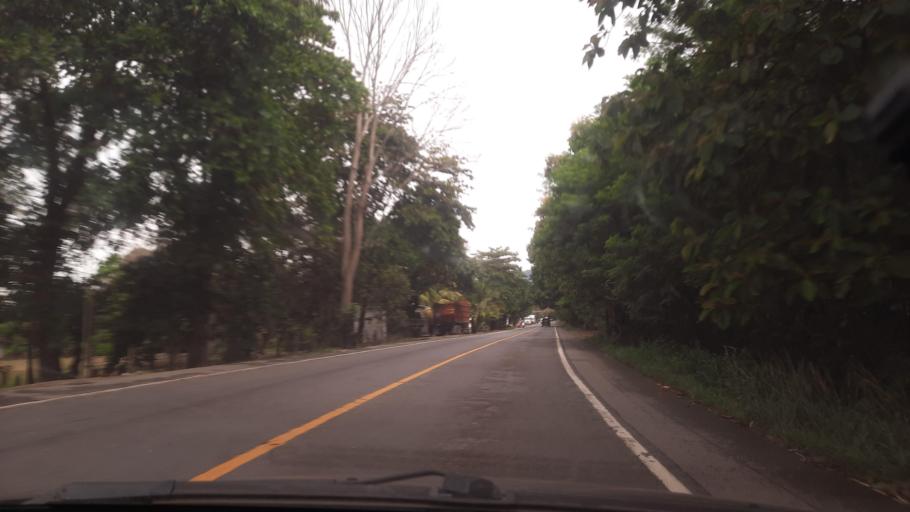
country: GT
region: Izabal
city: Morales
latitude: 15.4642
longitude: -88.9114
